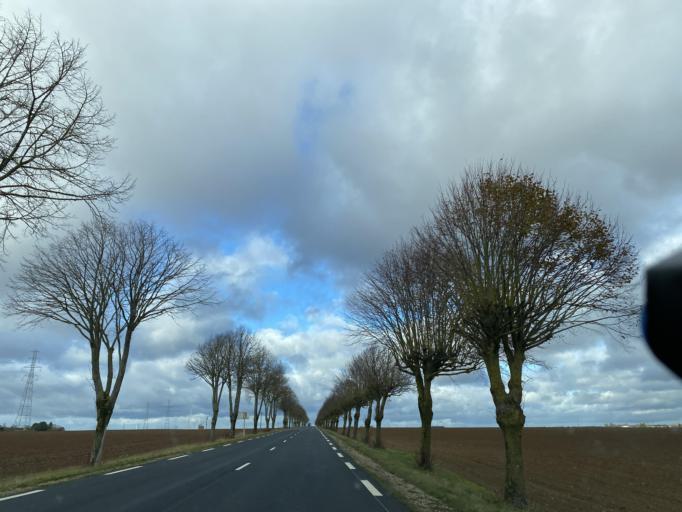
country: FR
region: Centre
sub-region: Departement d'Eure-et-Loir
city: Baigneaux
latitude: 48.1728
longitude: 1.8363
